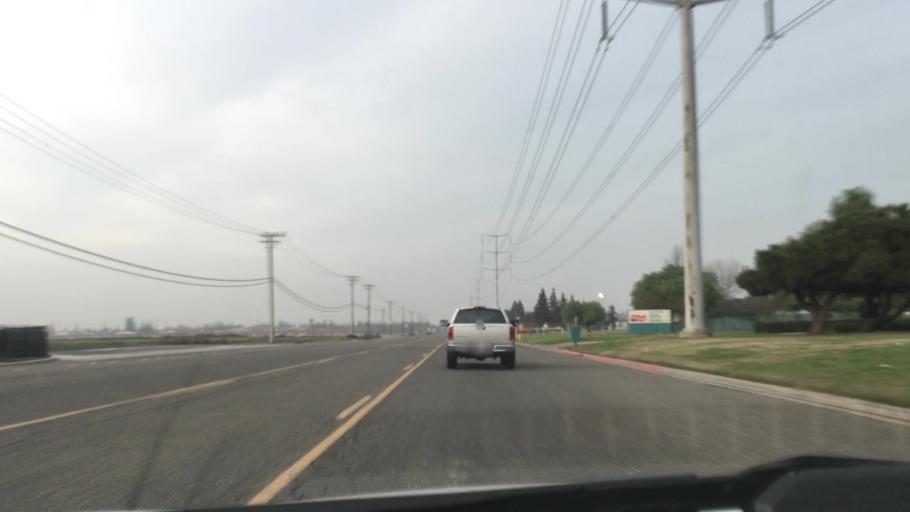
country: US
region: California
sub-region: Stanislaus County
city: Empire
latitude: 37.6310
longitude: -120.9231
